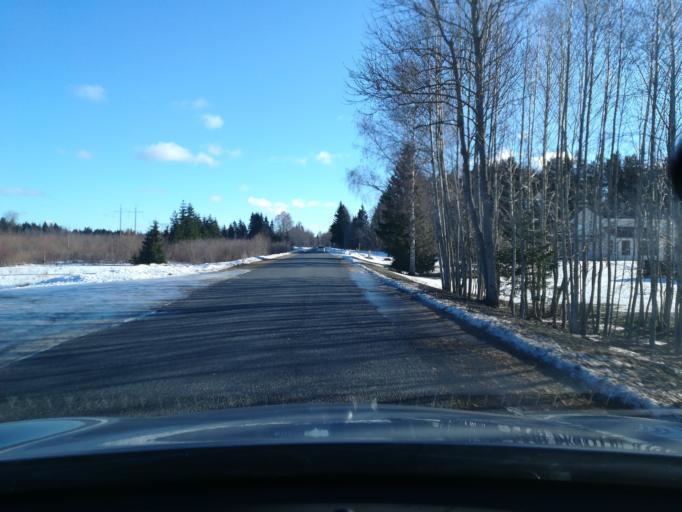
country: EE
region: Raplamaa
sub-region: Kohila vald
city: Kohila
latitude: 59.2343
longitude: 24.7620
